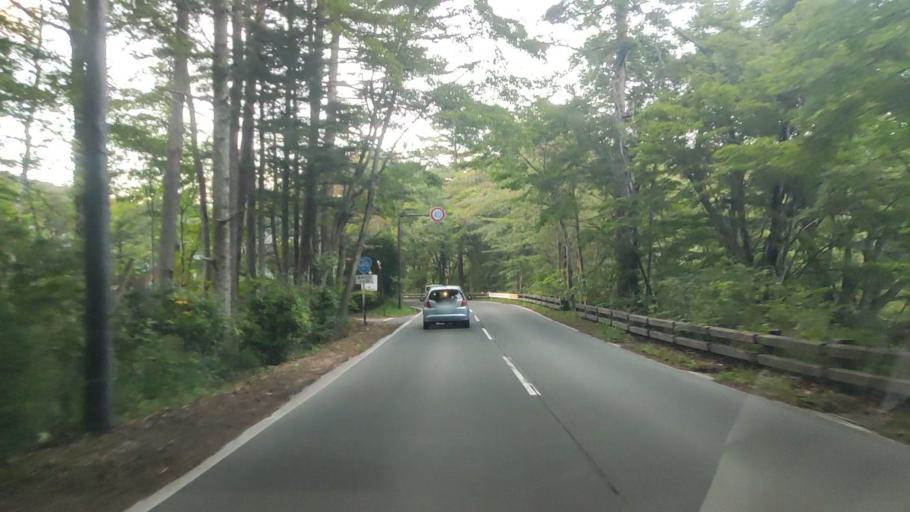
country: JP
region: Nagano
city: Komoro
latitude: 36.3767
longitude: 138.5868
